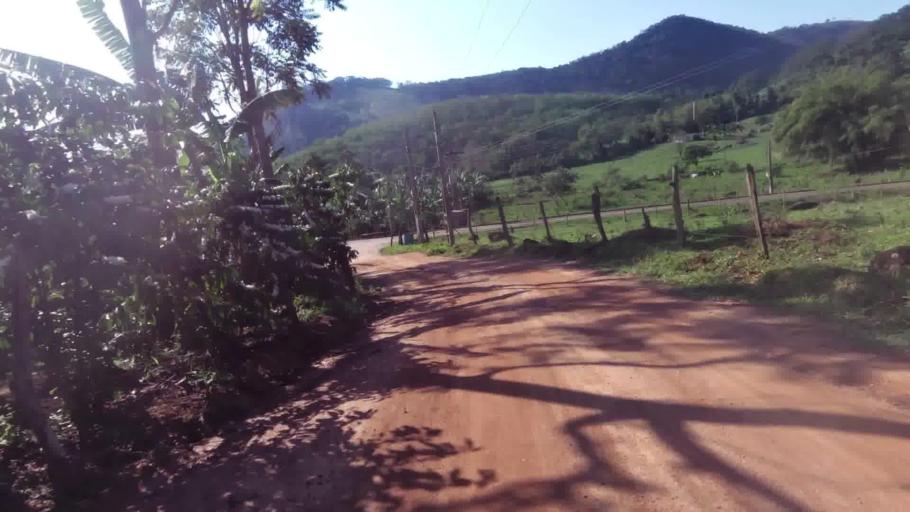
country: BR
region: Espirito Santo
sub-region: Alfredo Chaves
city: Alfredo Chaves
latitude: -20.6883
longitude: -40.7777
